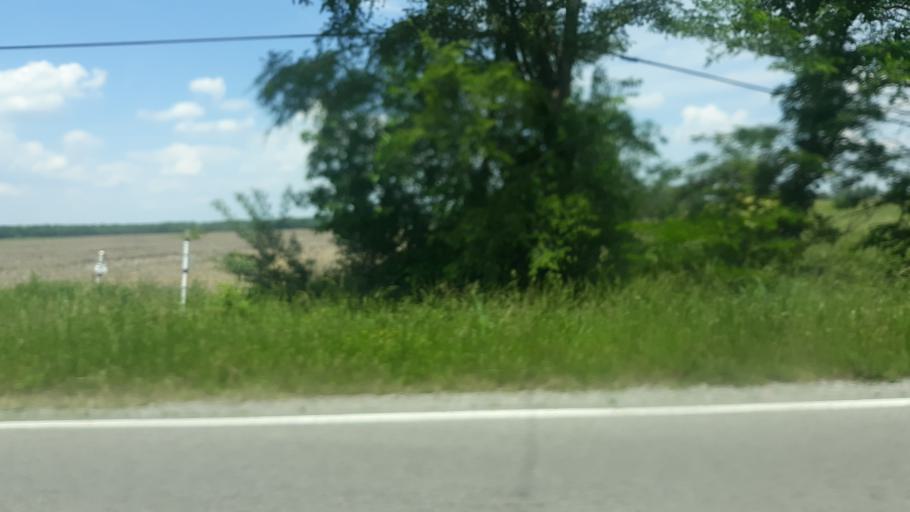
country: US
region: Illinois
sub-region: Saline County
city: Harrisburg
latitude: 37.6365
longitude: -88.5091
